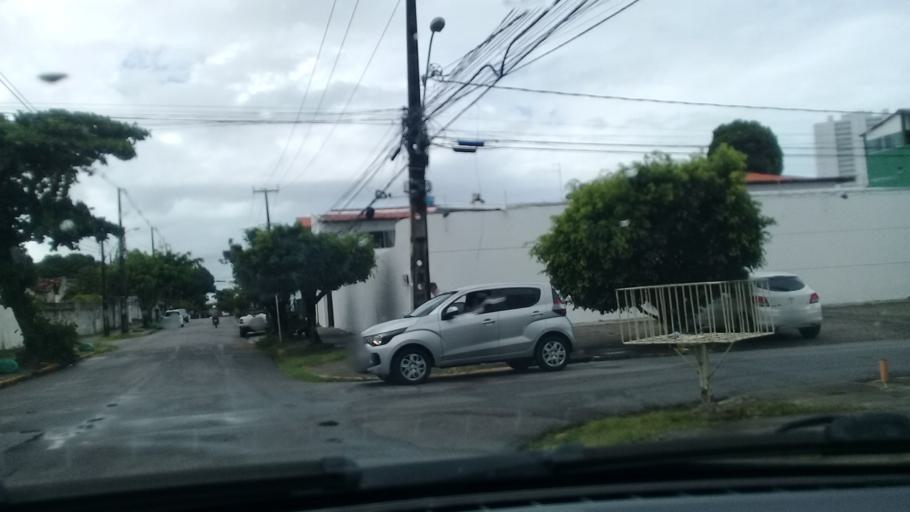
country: BR
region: Pernambuco
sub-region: Recife
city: Recife
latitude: -8.1364
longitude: -34.9139
